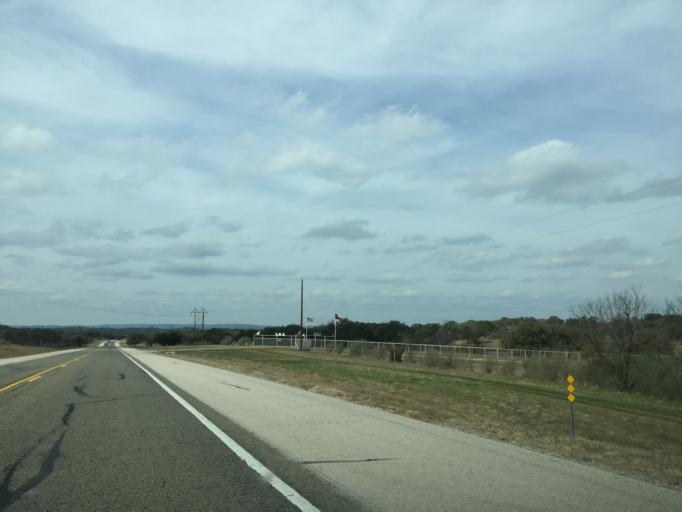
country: US
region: Texas
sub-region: Burnet County
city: Granite Shoals
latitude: 30.5306
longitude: -98.4303
